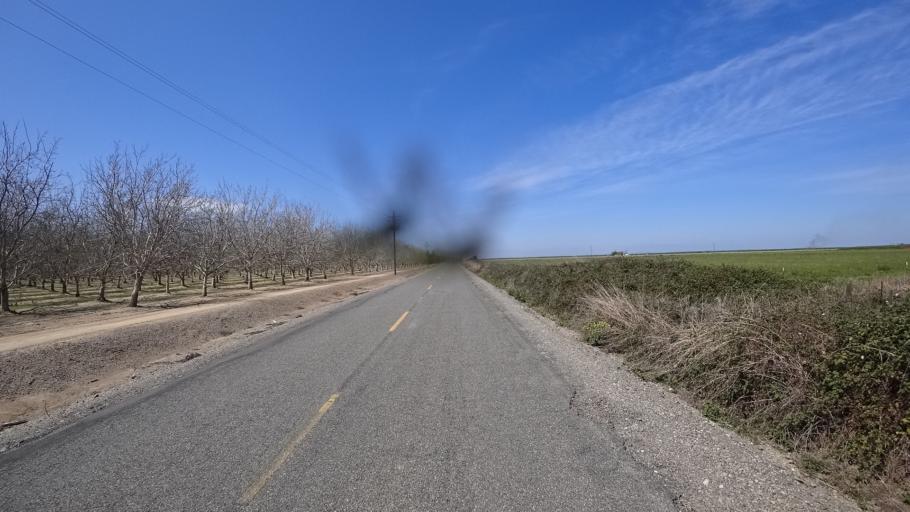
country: US
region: California
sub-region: Glenn County
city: Hamilton City
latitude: 39.6525
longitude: -122.0999
